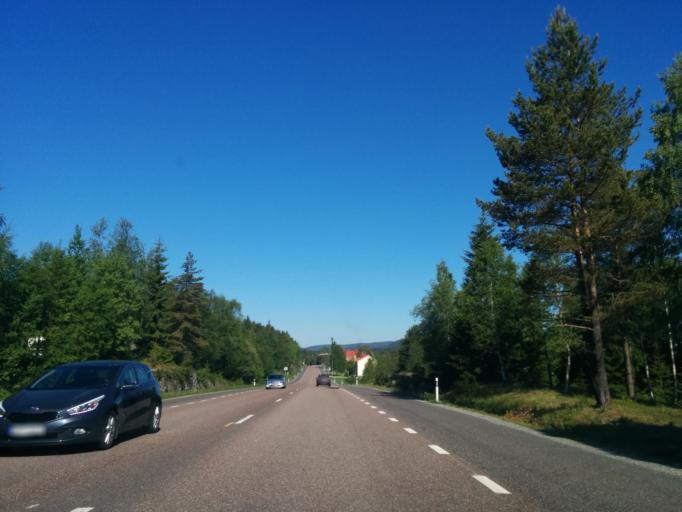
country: SE
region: Vaesternorrland
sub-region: Kramfors Kommun
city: Kramfors
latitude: 62.9062
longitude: 17.8233
